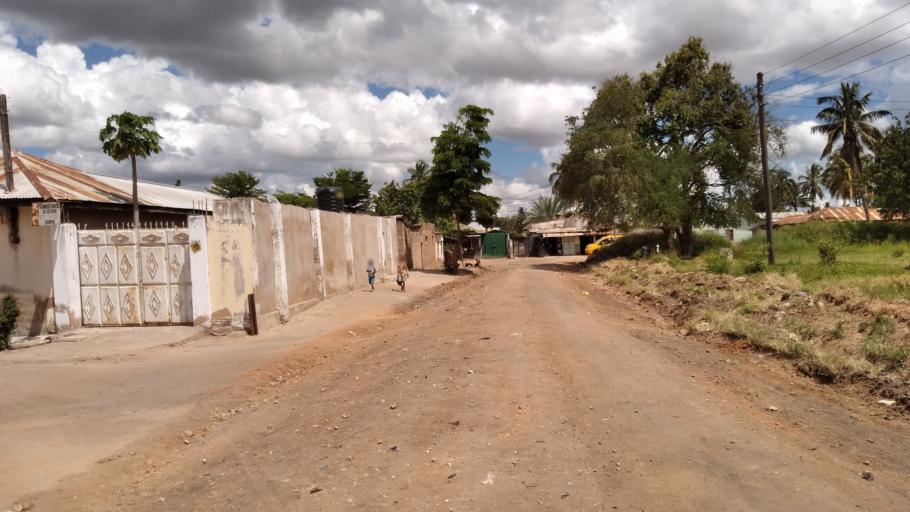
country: TZ
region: Dodoma
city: Dodoma
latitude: -6.1652
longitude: 35.7385
